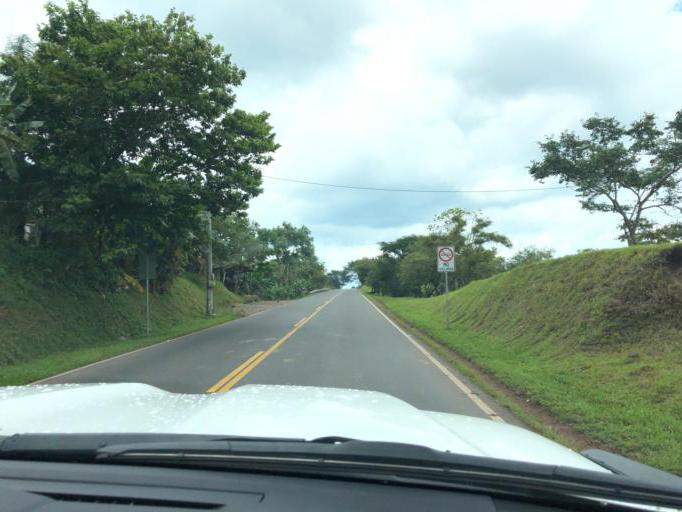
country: NI
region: Chontales
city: Villa Sandino
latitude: 11.9936
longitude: -84.8593
